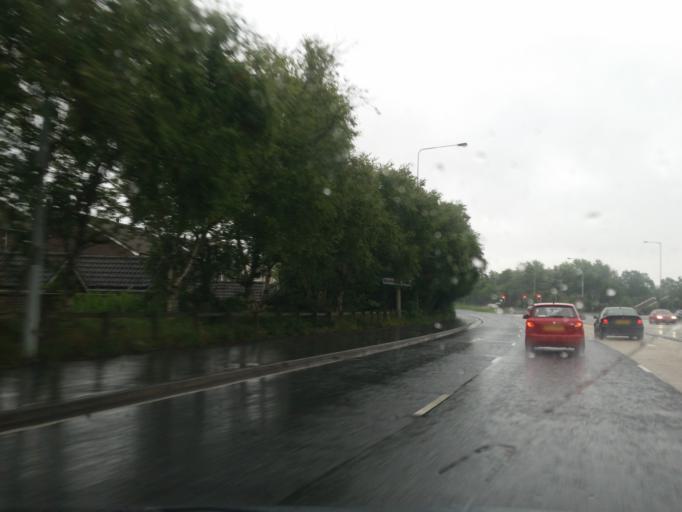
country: GB
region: Northern Ireland
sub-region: North Down District
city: Bangor
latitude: 54.6469
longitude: -5.7136
